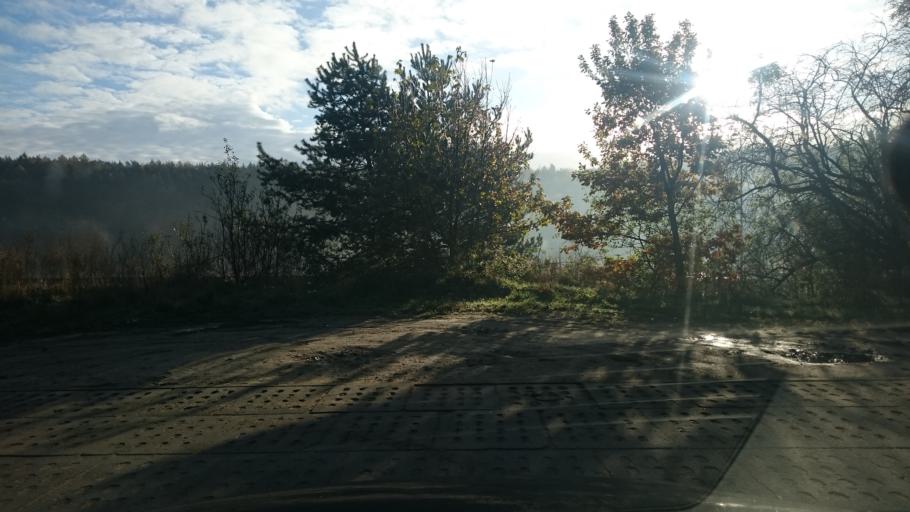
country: PL
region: Pomeranian Voivodeship
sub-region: Gdynia
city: Wielki Kack
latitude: 54.4605
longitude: 18.4946
